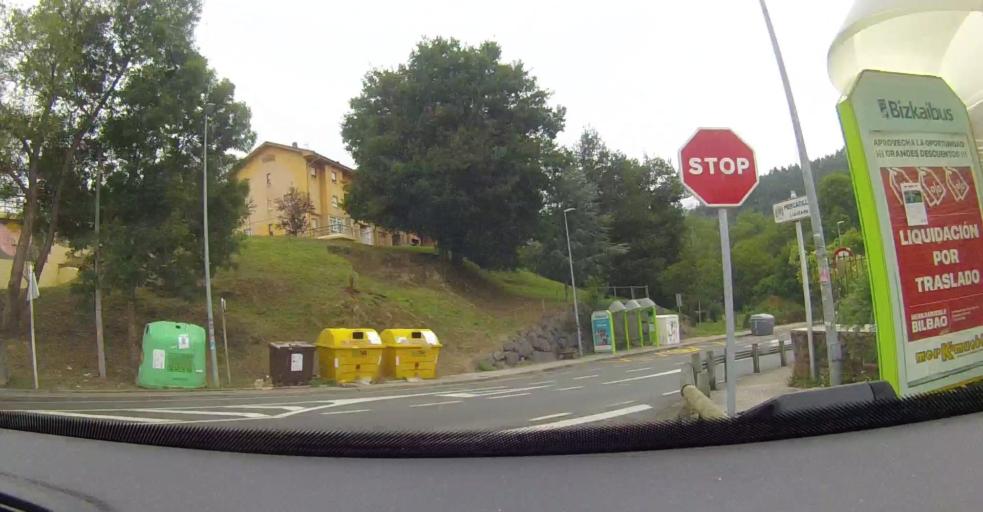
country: ES
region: Basque Country
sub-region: Bizkaia
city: Sopuerta
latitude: 43.2620
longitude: -3.1541
